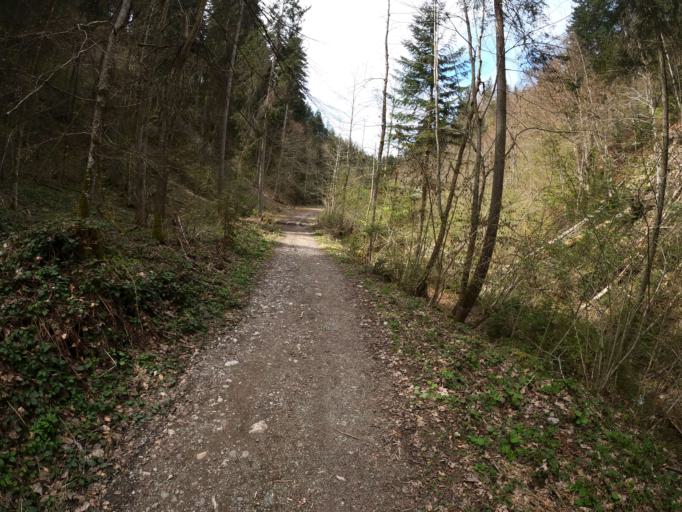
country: AT
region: Salzburg
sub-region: Politischer Bezirk Sankt Johann im Pongau
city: Pfarrwerfen
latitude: 47.4602
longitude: 13.2223
